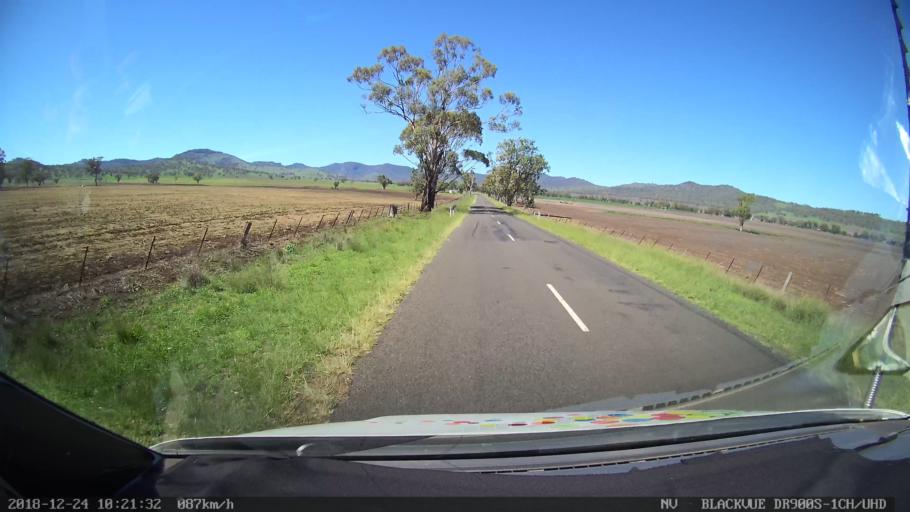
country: AU
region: New South Wales
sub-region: Liverpool Plains
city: Quirindi
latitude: -31.7533
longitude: 150.5501
